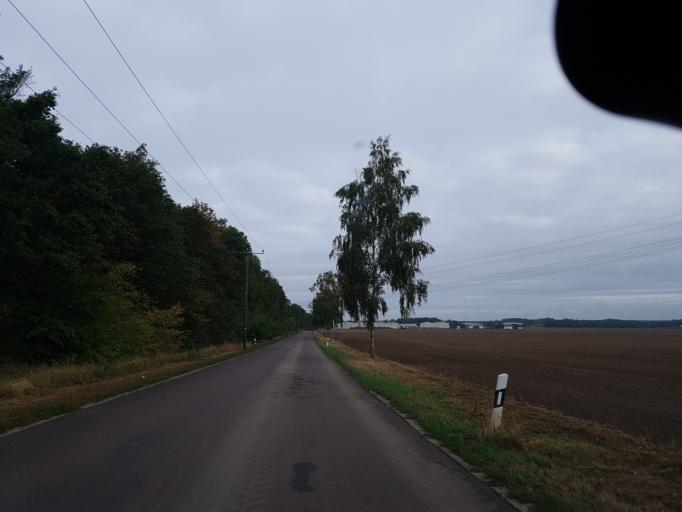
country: DE
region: Saxony-Anhalt
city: Klieken
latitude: 51.9431
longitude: 12.3156
